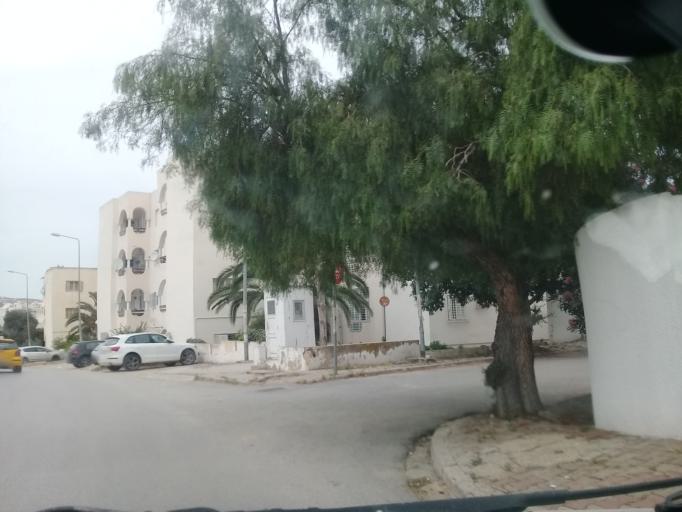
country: TN
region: Tunis
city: Tunis
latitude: 36.8438
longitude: 10.1587
